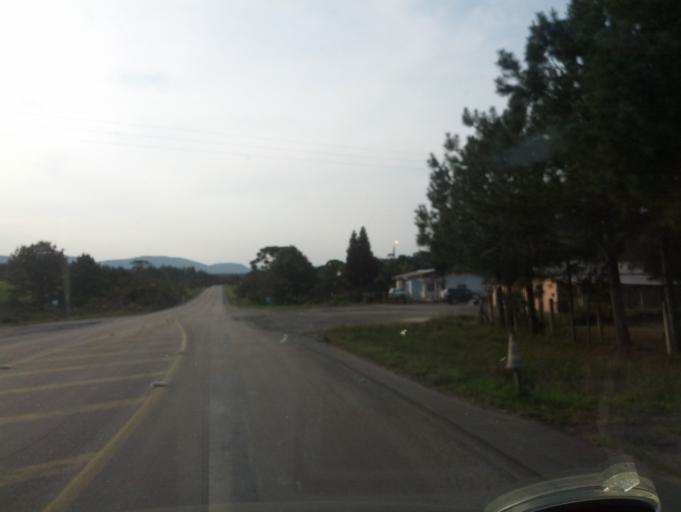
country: BR
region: Santa Catarina
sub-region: Otacilio Costa
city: Otacilio Costa
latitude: -27.4039
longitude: -50.1307
